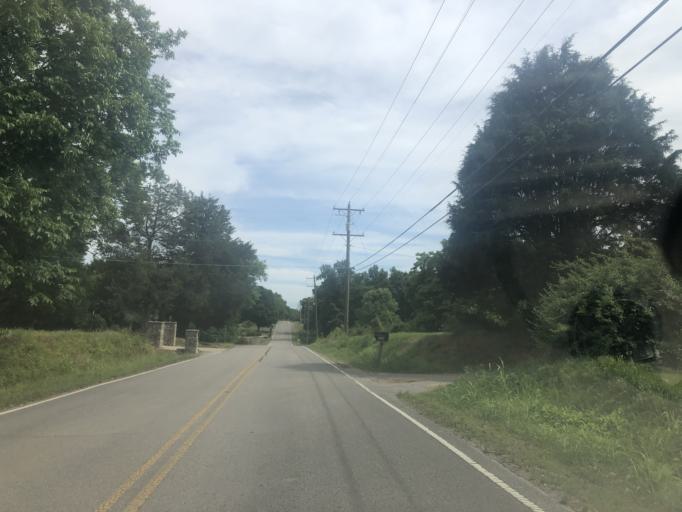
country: US
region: Tennessee
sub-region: Davidson County
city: Lakewood
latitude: 36.2132
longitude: -86.6663
